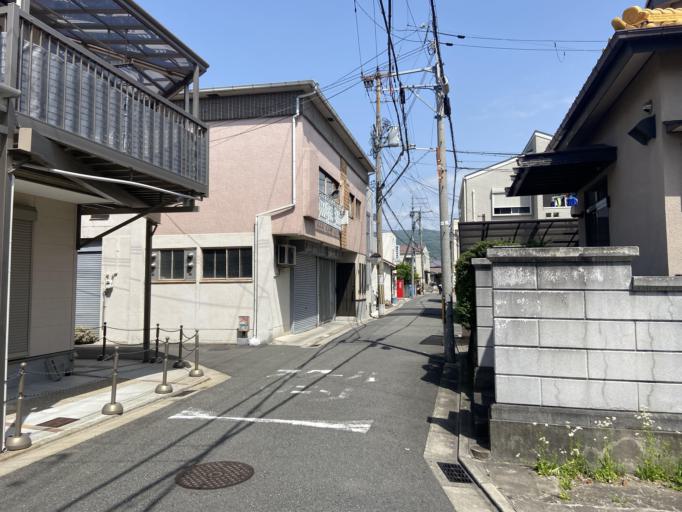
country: JP
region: Osaka
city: Daitocho
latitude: 34.6717
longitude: 135.6102
